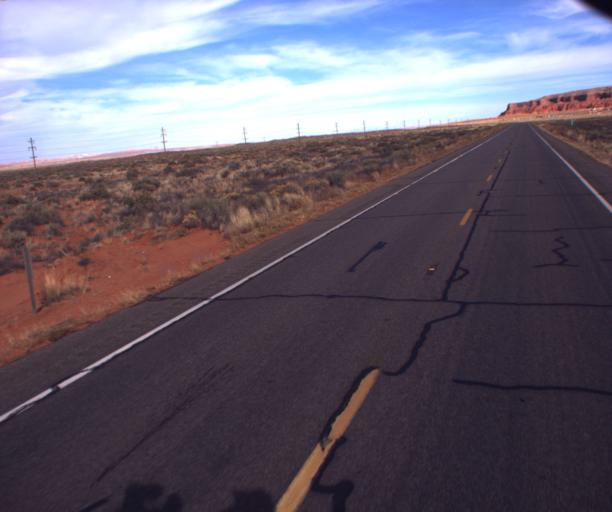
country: US
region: Arizona
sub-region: Navajo County
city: Kayenta
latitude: 36.7840
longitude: -109.9730
